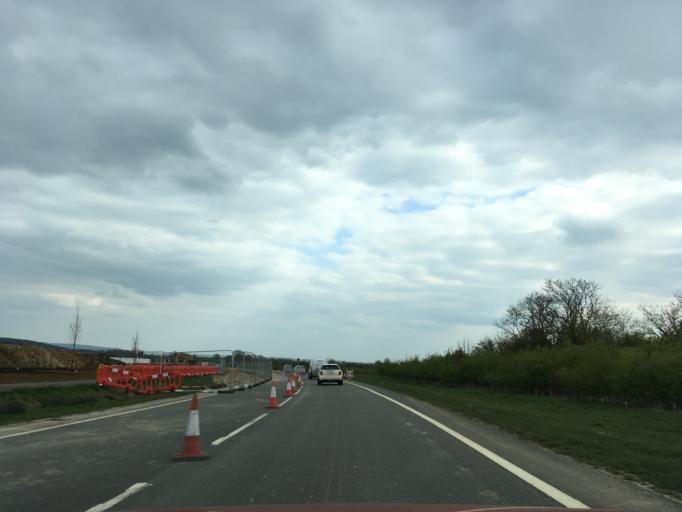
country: GB
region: England
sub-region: Oxfordshire
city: Bicester
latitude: 51.8957
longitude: -1.1828
